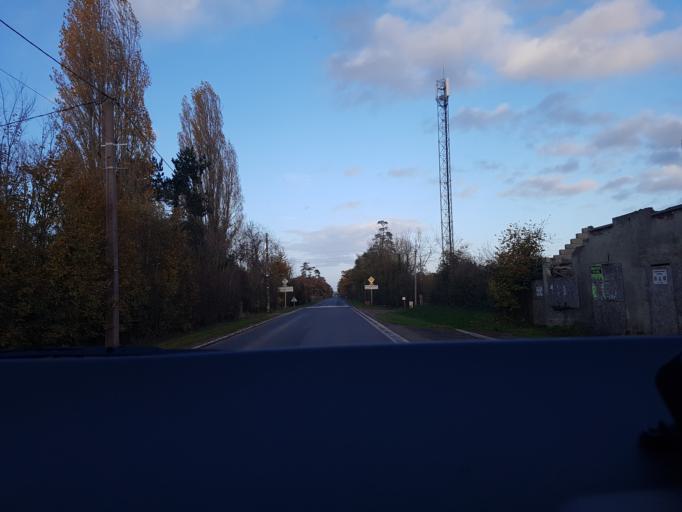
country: FR
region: Lower Normandy
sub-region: Departement du Calvados
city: Dozule
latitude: 49.2125
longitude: -0.1118
